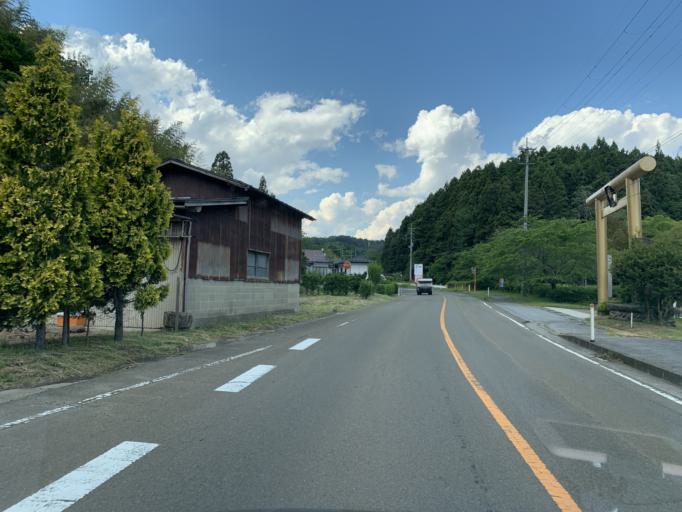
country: JP
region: Miyagi
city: Wakuya
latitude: 38.5577
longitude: 141.1363
